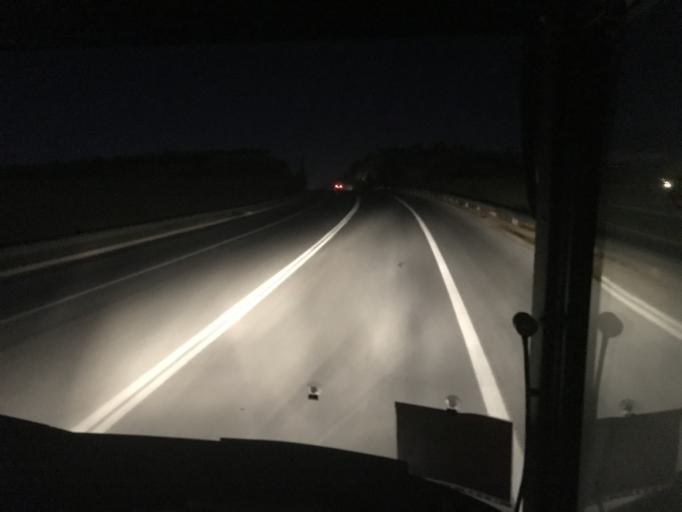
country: GR
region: Crete
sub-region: Nomos Irakleiou
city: Skalanion
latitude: 35.2761
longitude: 25.1826
